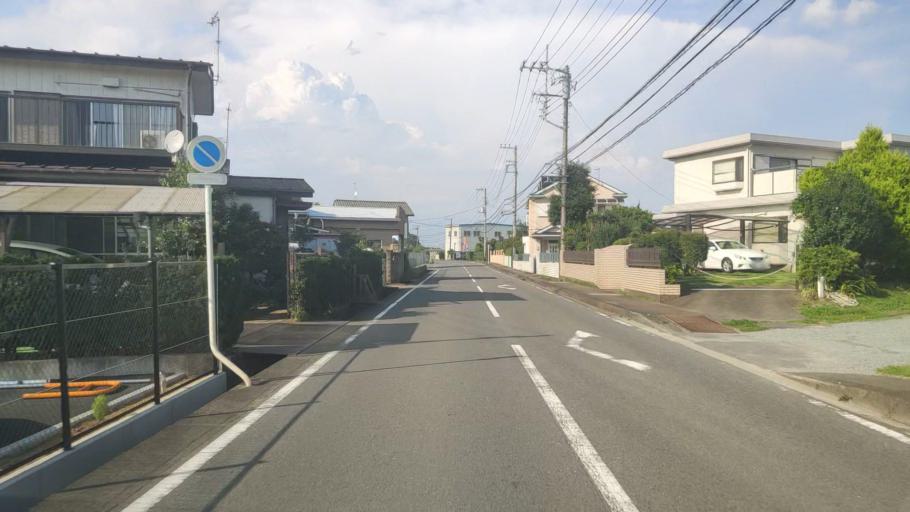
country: JP
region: Kanagawa
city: Isehara
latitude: 35.3794
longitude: 139.3368
